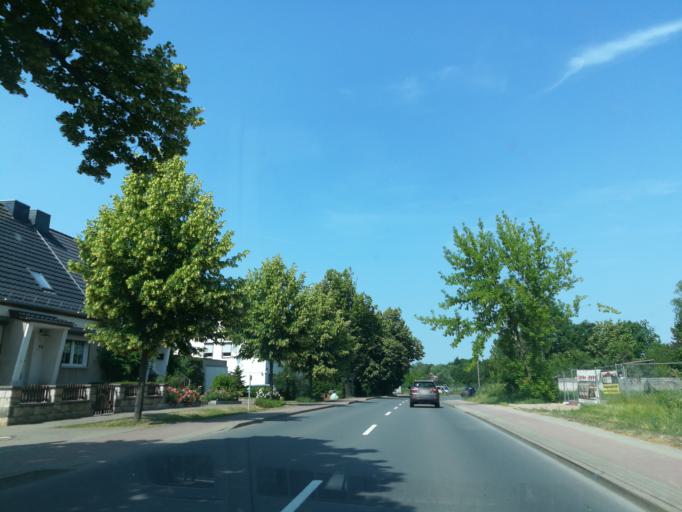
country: DE
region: Saxony-Anhalt
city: Aschersleben
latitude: 51.7691
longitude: 11.4522
